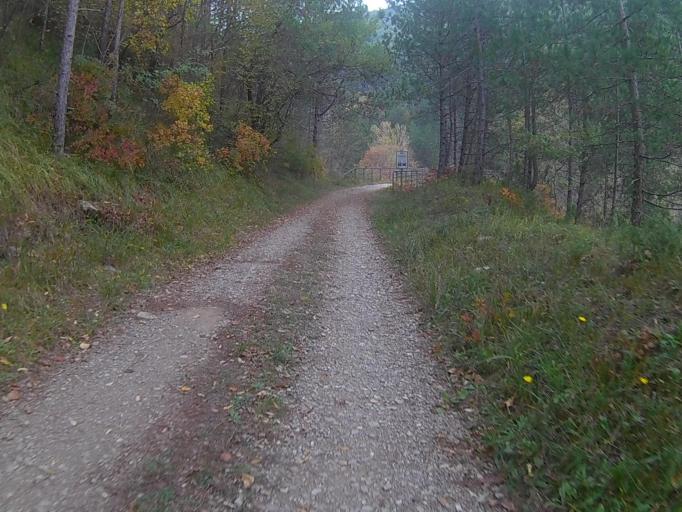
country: HR
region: Istarska
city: Karojba
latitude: 45.3736
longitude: 13.8027
